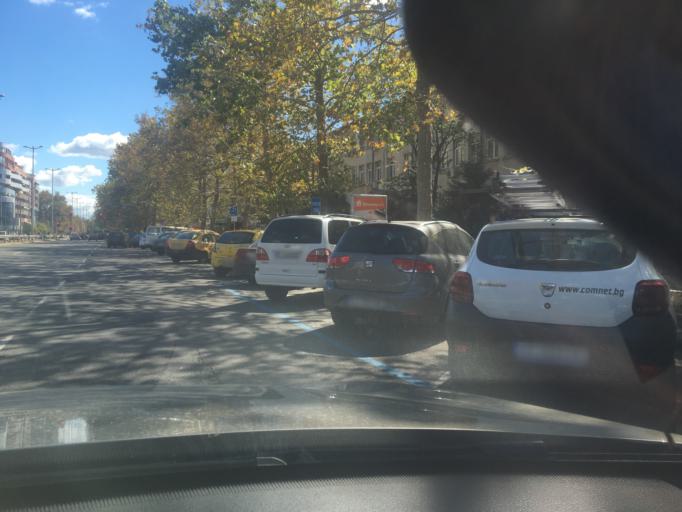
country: BG
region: Burgas
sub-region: Obshtina Burgas
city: Burgas
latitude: 42.5019
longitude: 27.4765
